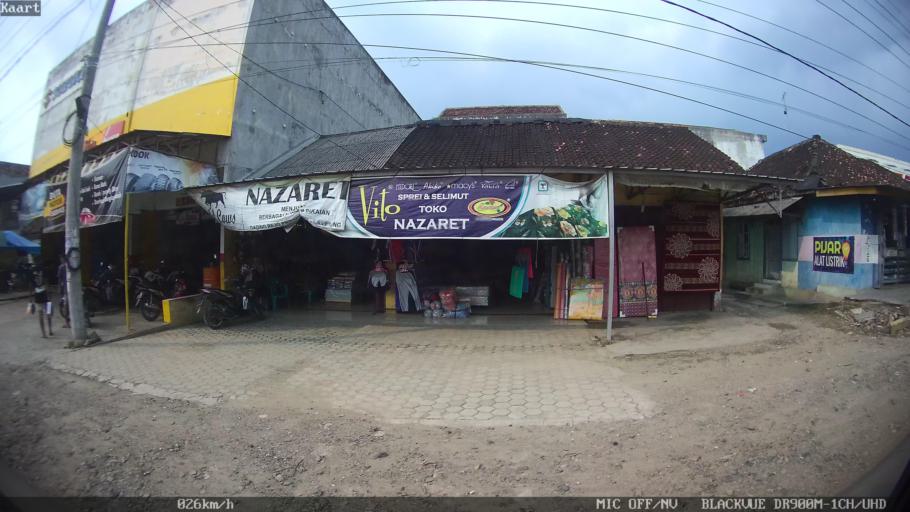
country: ID
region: Lampung
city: Gadingrejo
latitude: -5.3725
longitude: 105.0583
